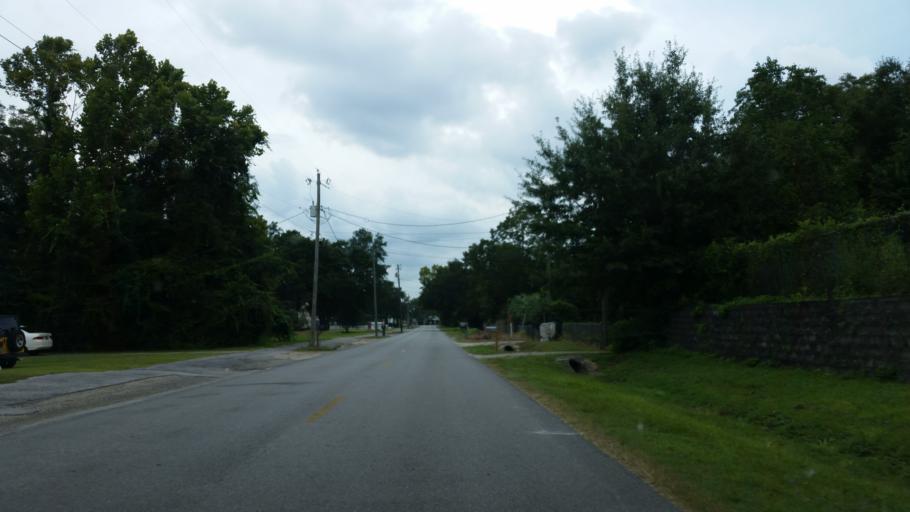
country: US
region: Florida
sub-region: Santa Rosa County
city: Pace
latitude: 30.6040
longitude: -87.1576
